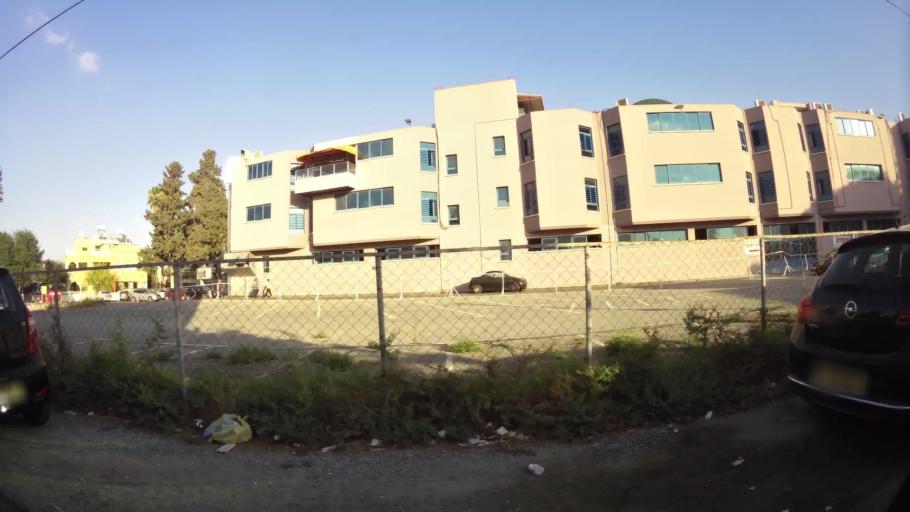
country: CY
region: Lefkosia
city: Nicosia
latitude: 35.1873
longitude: 33.3547
